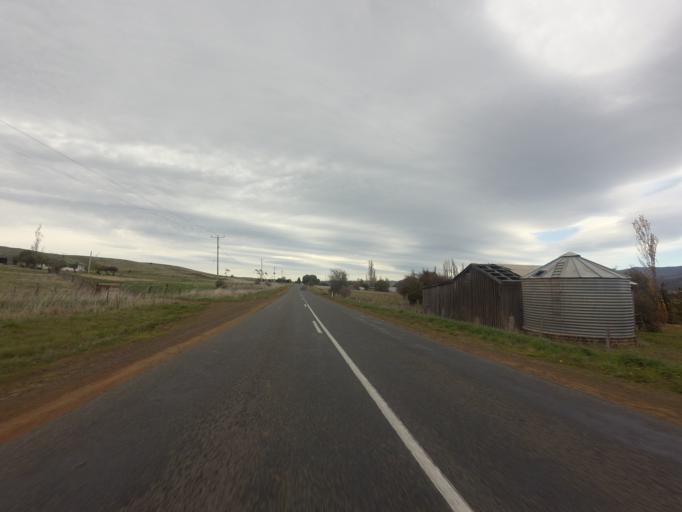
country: AU
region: Tasmania
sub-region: Derwent Valley
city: New Norfolk
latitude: -42.5074
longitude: 146.7386
